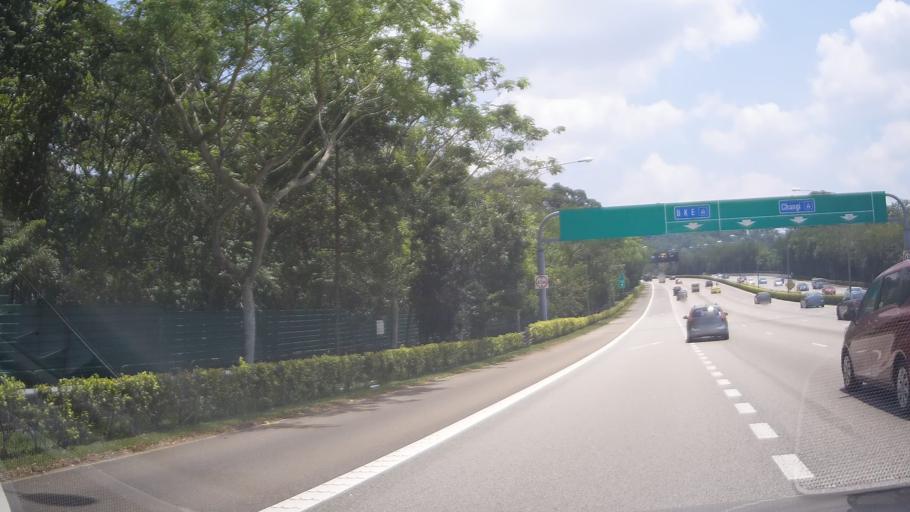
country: SG
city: Singapore
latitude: 1.3438
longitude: 103.7849
